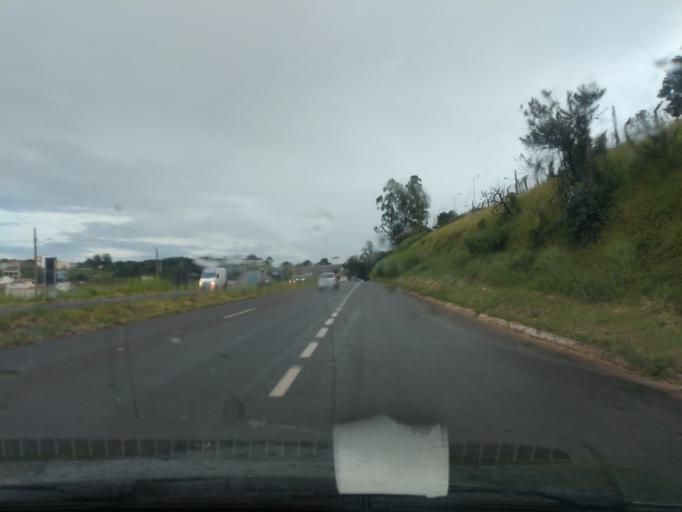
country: BR
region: Minas Gerais
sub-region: Varginha
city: Varginha
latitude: -21.5754
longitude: -45.4494
